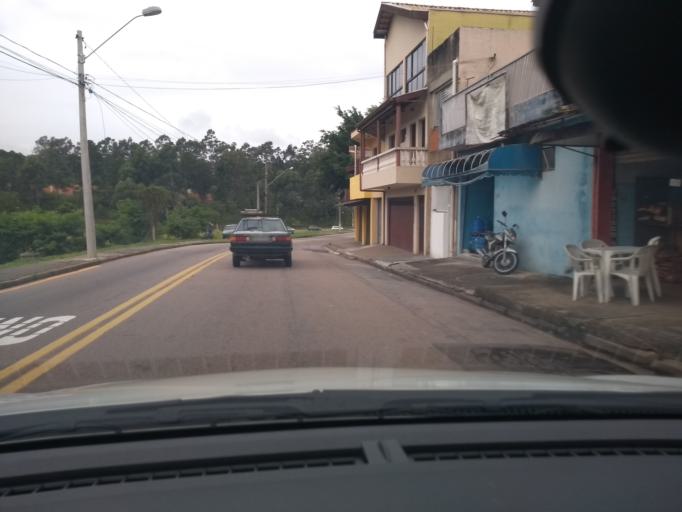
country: BR
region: Sao Paulo
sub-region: Jundiai
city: Jundiai
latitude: -23.1828
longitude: -46.9646
